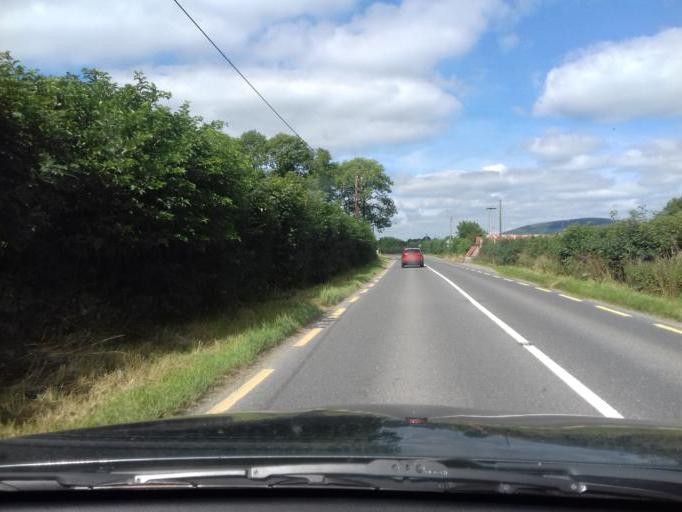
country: IE
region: Leinster
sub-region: Wicklow
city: Baltinglass
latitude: 53.0064
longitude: -6.6429
